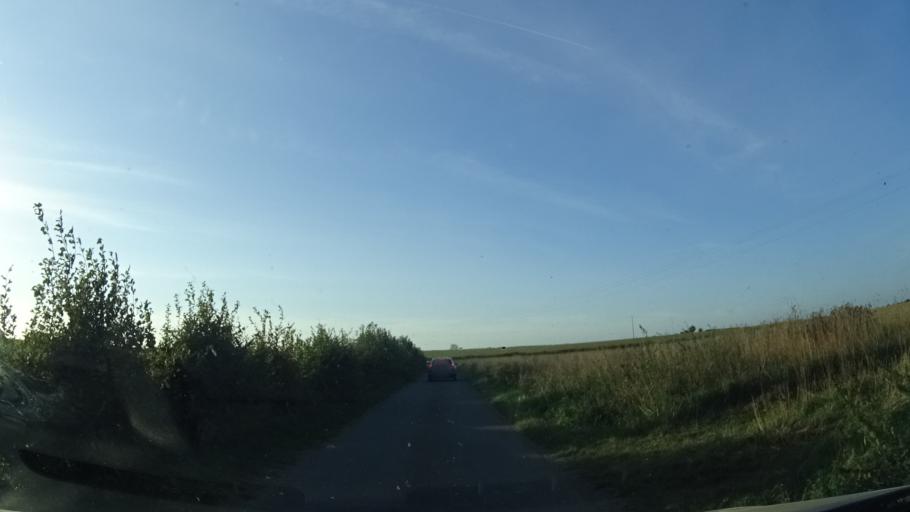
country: BE
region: Wallonia
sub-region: Province du Hainaut
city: Beaumont
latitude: 50.2428
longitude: 4.2664
